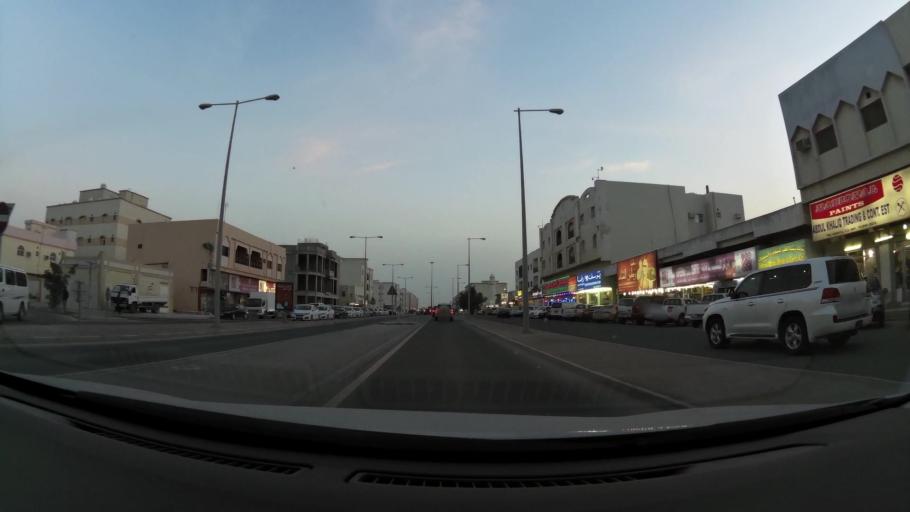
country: QA
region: Al Wakrah
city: Al Wakrah
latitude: 25.1533
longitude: 51.5989
